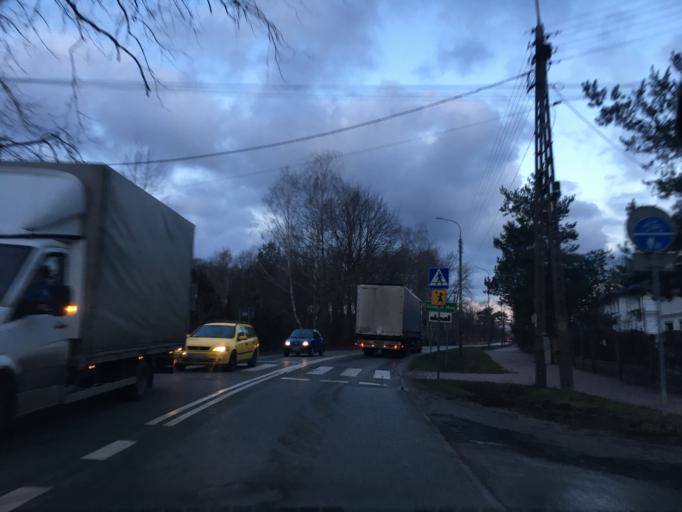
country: PL
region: Masovian Voivodeship
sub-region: Powiat grodziski
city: Milanowek
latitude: 52.0940
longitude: 20.6624
